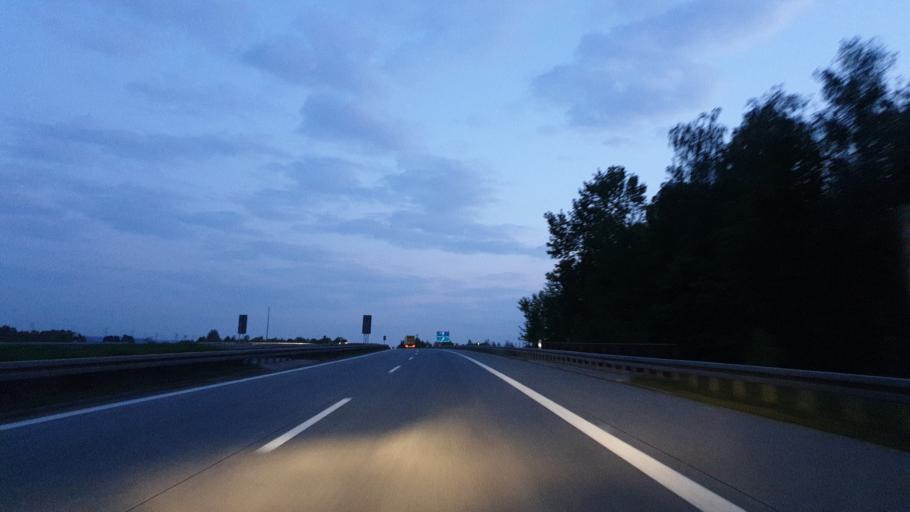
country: DE
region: Saxony
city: Neukirchen
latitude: 50.7852
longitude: 12.8290
